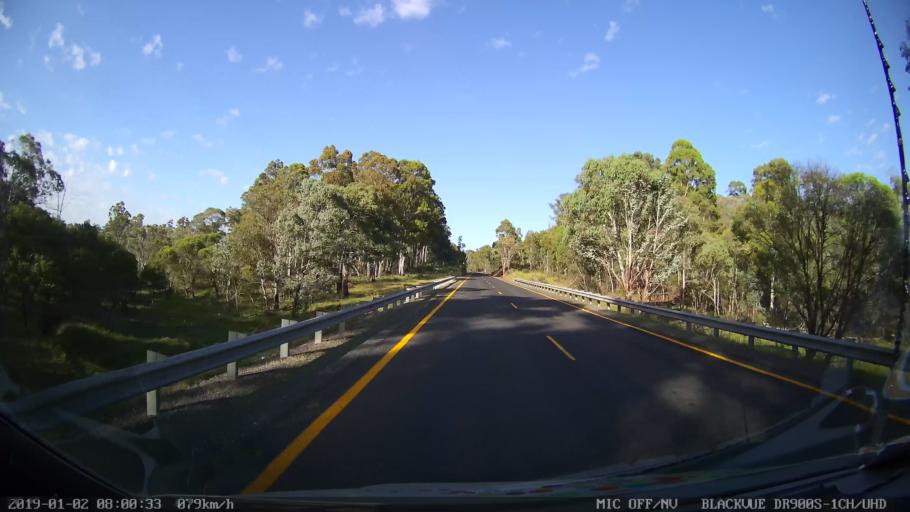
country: AU
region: New South Wales
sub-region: Tumut Shire
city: Tumut
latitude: -35.6448
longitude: 148.4437
